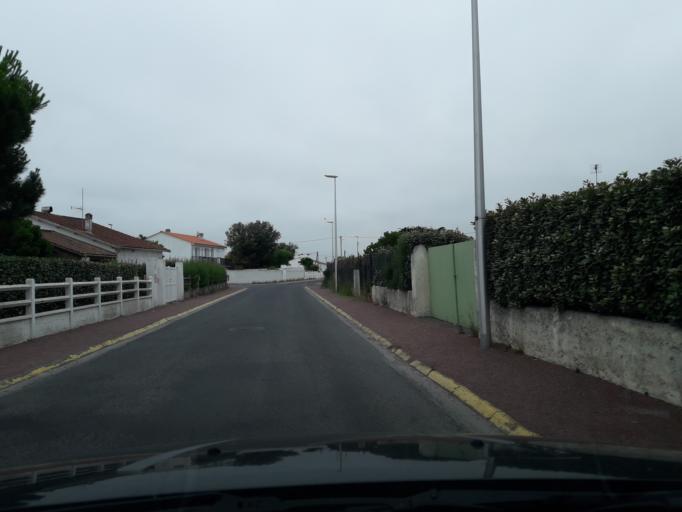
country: FR
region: Poitou-Charentes
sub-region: Departement de la Charente-Maritime
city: Boyard-Ville
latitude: 45.9673
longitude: -1.2441
